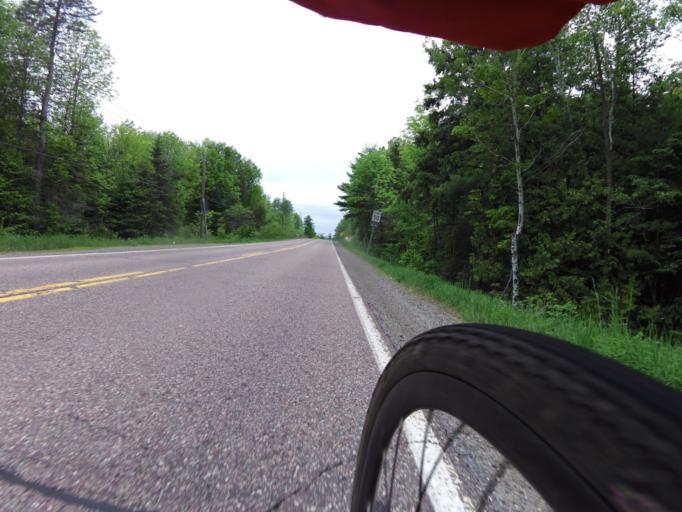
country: CA
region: Ontario
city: Renfrew
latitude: 45.2966
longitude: -76.7122
